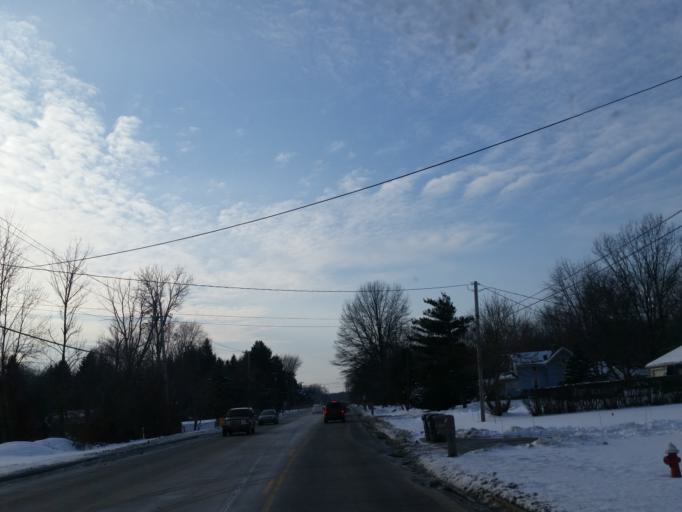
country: US
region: Ohio
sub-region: Lorain County
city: Sheffield Lake
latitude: 41.4655
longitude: -82.0784
